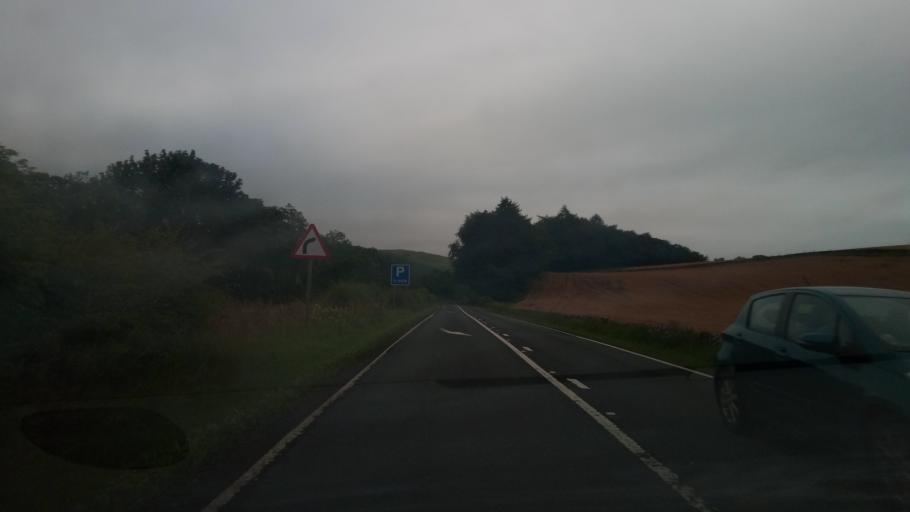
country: GB
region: Scotland
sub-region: The Scottish Borders
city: Hawick
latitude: 55.4044
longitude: -2.8325
